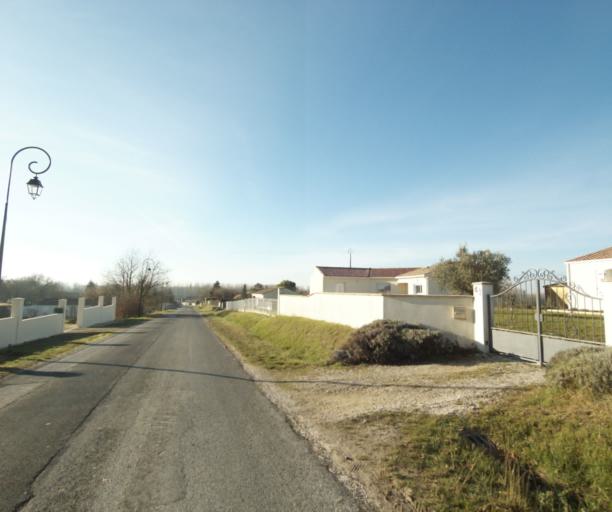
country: FR
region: Poitou-Charentes
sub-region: Departement de la Charente-Maritime
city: Cherac
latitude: 45.6894
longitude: -0.4505
